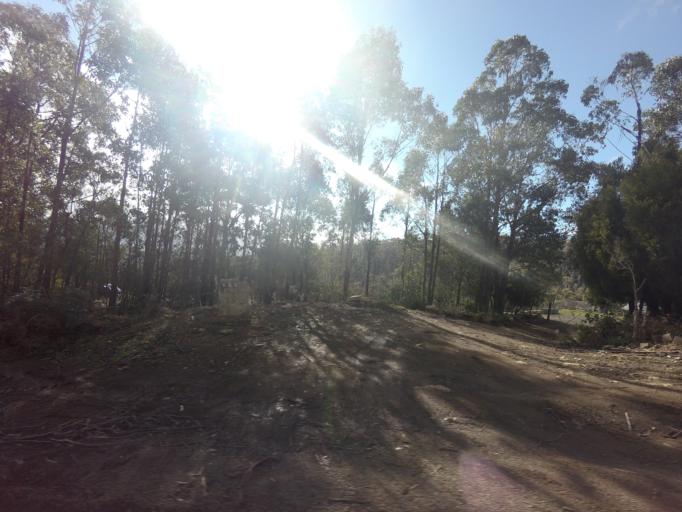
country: AU
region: Tasmania
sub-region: Derwent Valley
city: New Norfolk
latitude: -42.8351
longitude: 147.1312
